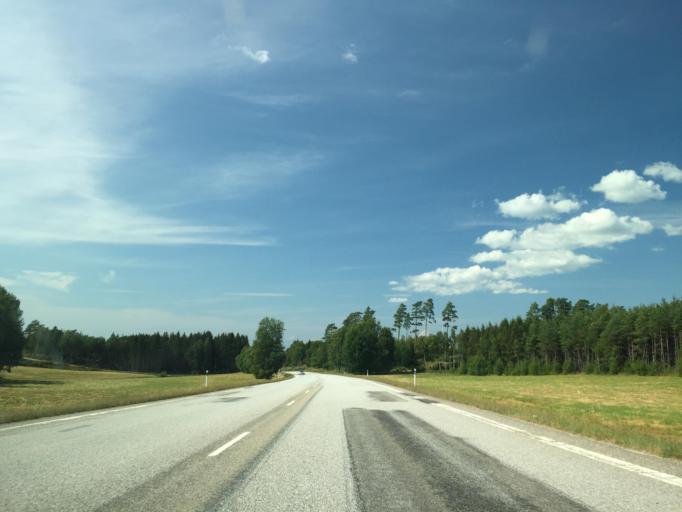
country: SE
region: Vaestra Goetaland
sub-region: Tanums Kommun
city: Tanumshede
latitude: 58.7553
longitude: 11.2799
